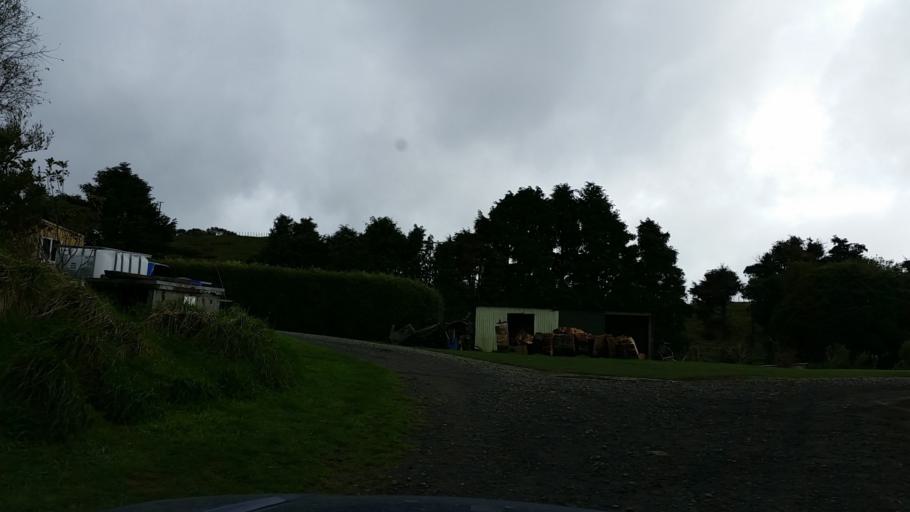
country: NZ
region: Taranaki
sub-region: South Taranaki District
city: Eltham
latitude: -39.4384
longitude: 174.6421
